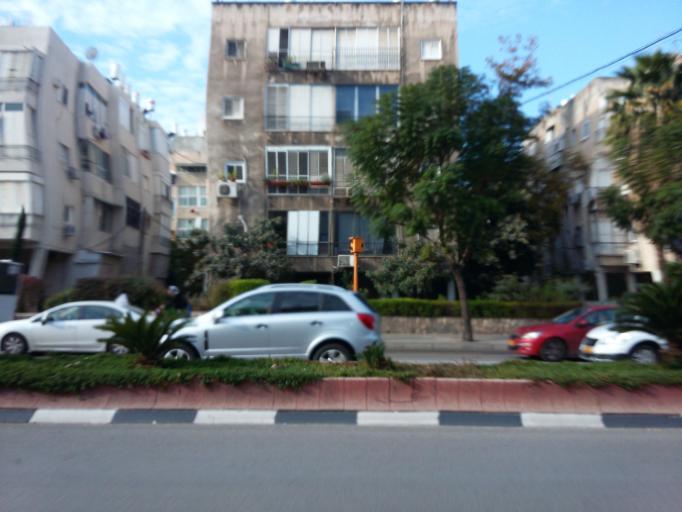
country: IL
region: Tel Aviv
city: Tel Aviv
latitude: 32.0944
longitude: 34.7944
